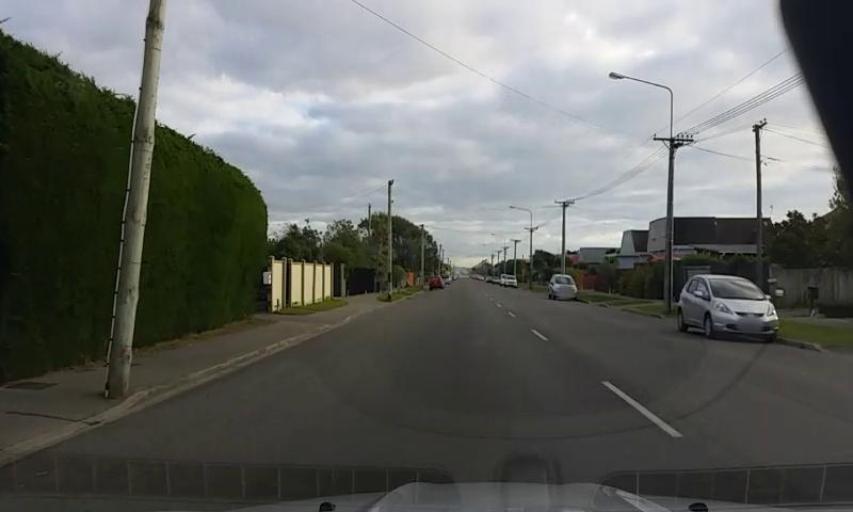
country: NZ
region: Canterbury
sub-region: Christchurch City
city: Christchurch
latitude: -43.5297
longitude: 172.7354
